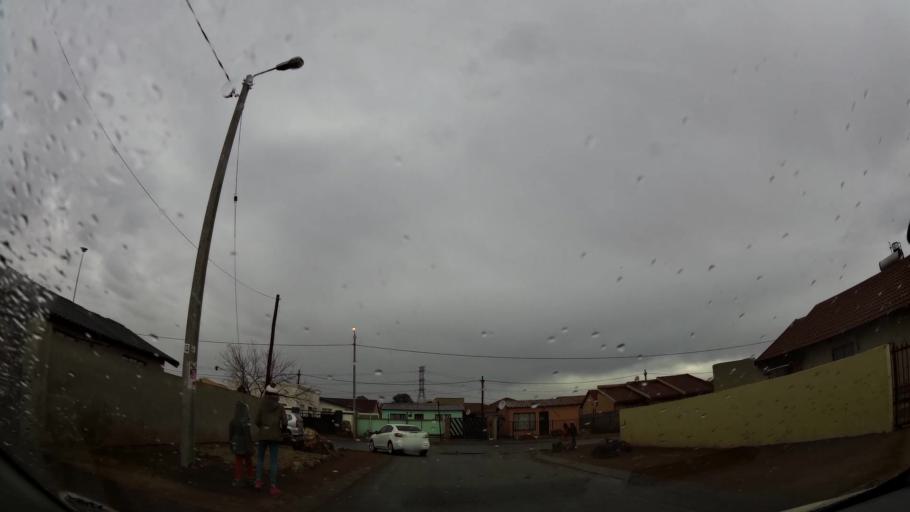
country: ZA
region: Gauteng
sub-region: Ekurhuleni Metropolitan Municipality
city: Germiston
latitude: -26.3402
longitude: 28.2053
